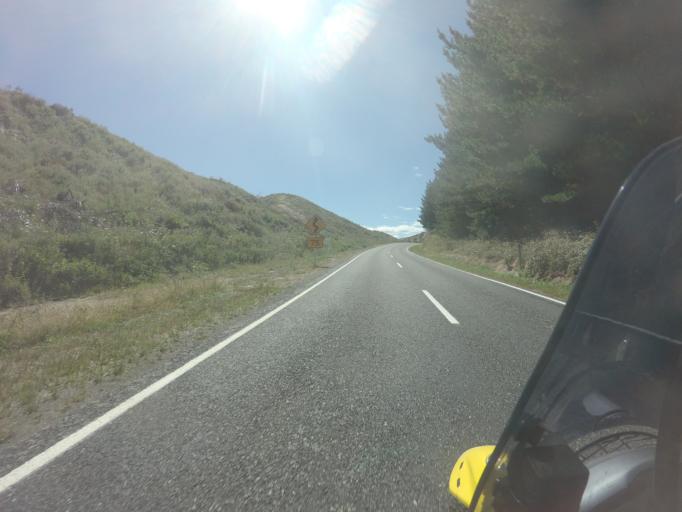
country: NZ
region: Bay of Plenty
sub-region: Whakatane District
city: Murupara
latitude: -38.3137
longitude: 176.8035
